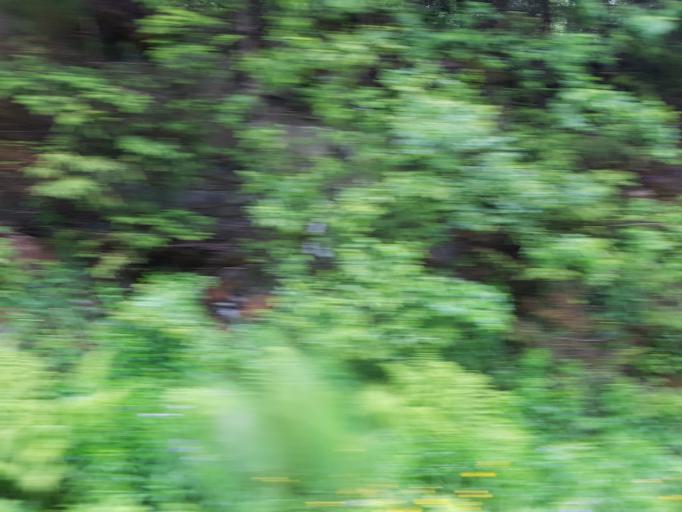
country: NO
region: Sor-Trondelag
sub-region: Selbu
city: Mebonden
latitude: 63.3673
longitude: 11.0741
